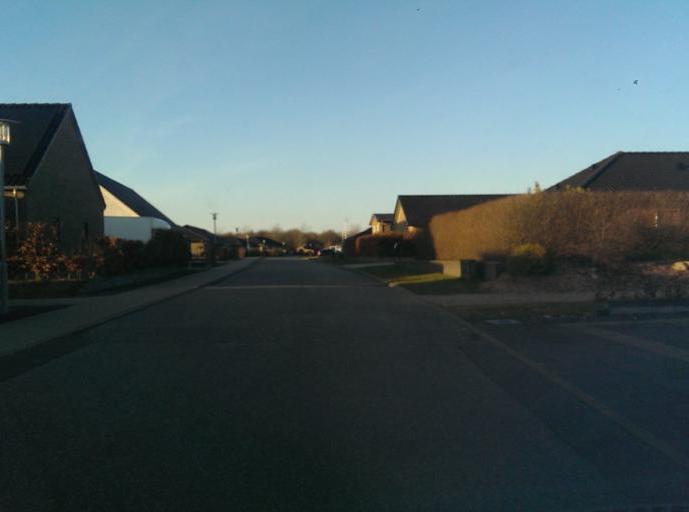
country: DK
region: South Denmark
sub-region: Esbjerg Kommune
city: Esbjerg
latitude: 55.5280
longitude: 8.4086
